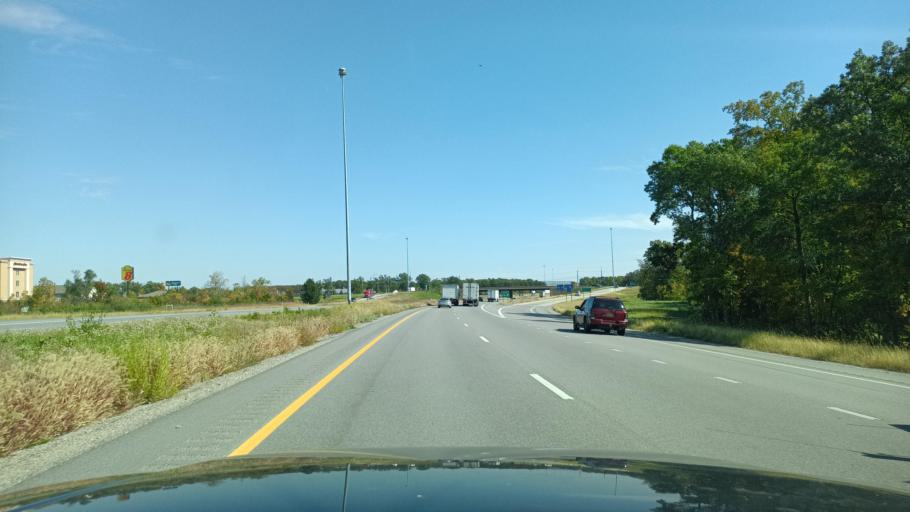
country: US
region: Ohio
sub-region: Defiance County
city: Defiance
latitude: 41.3073
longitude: -84.3661
